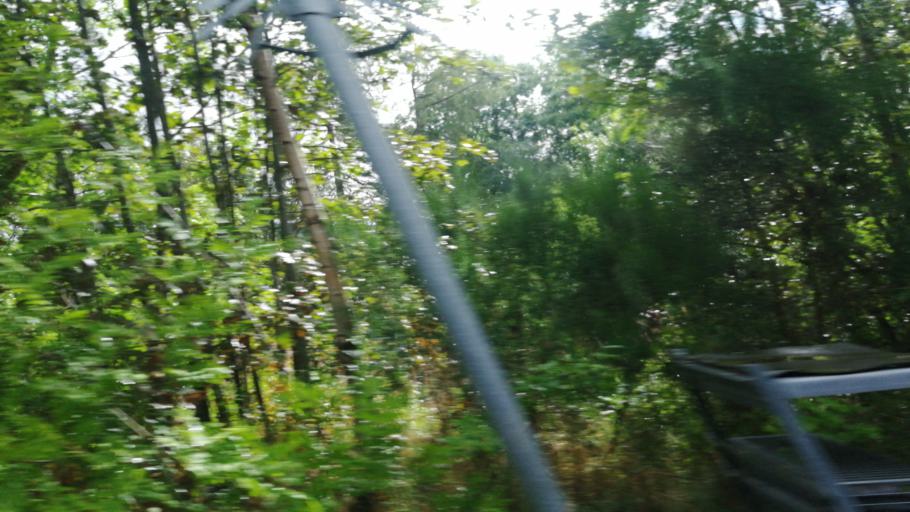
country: GB
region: Scotland
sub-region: Aberdeenshire
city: Insch
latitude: 57.3222
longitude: -2.5448
